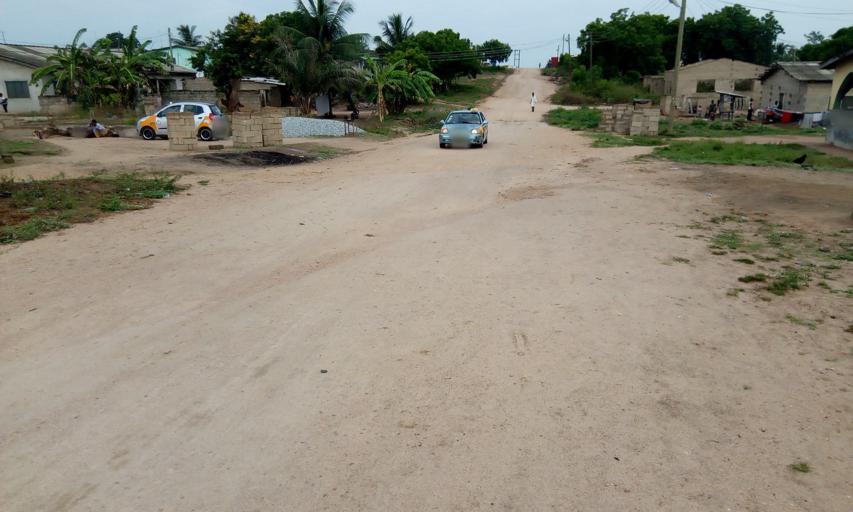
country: GH
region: Central
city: Winneba
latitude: 5.3562
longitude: -0.6169
